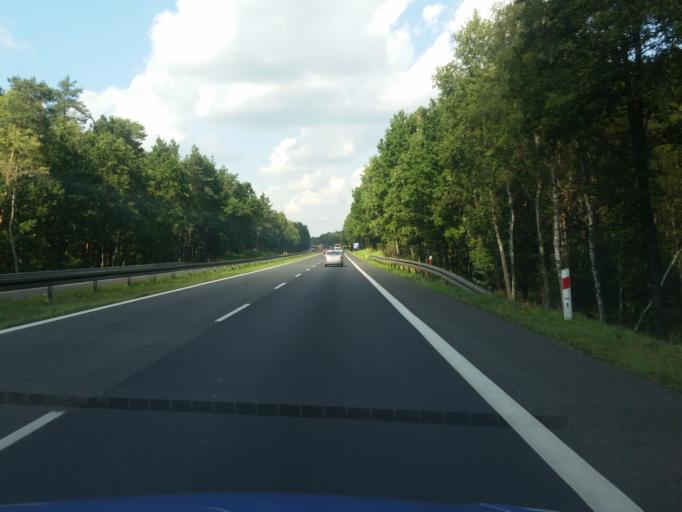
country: PL
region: Silesian Voivodeship
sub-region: Powiat czestochowski
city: Kamienica Polska
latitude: 50.6539
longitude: 19.1320
